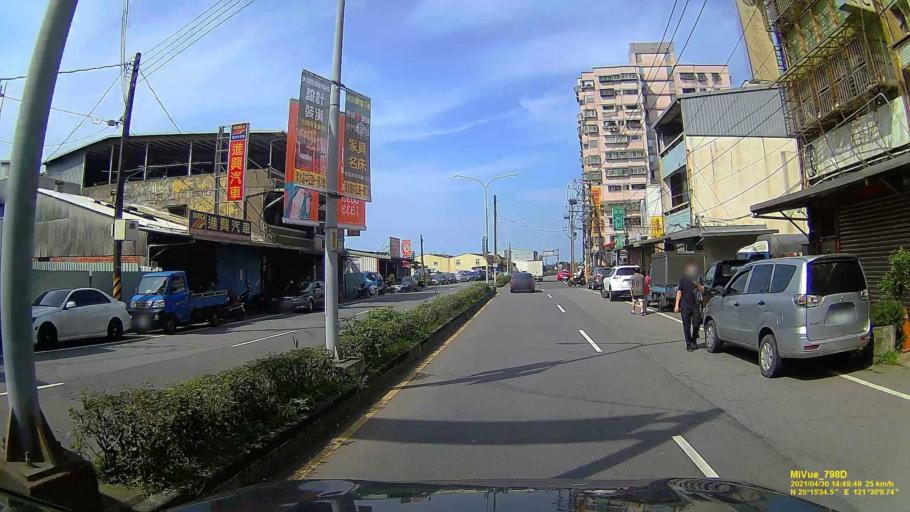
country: TW
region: Taipei
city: Taipei
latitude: 25.2597
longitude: 121.5028
